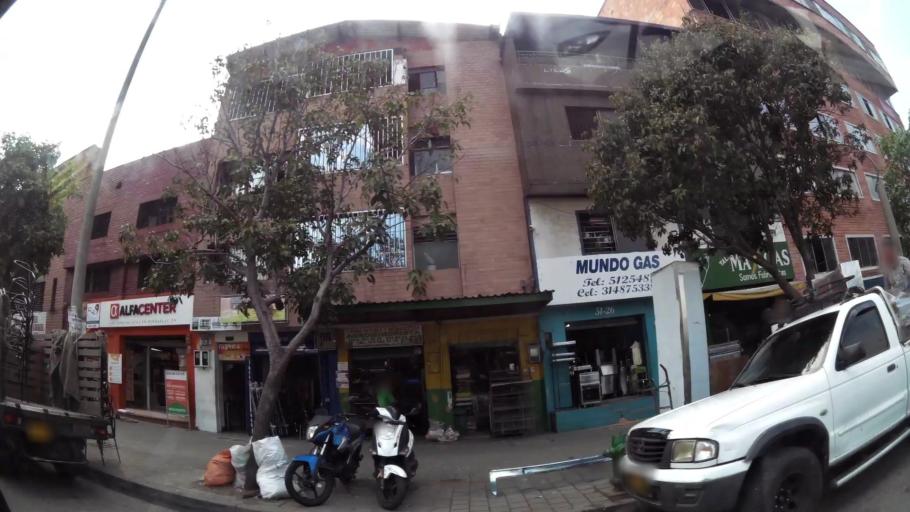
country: CO
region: Antioquia
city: Medellin
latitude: 6.2547
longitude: -75.5745
